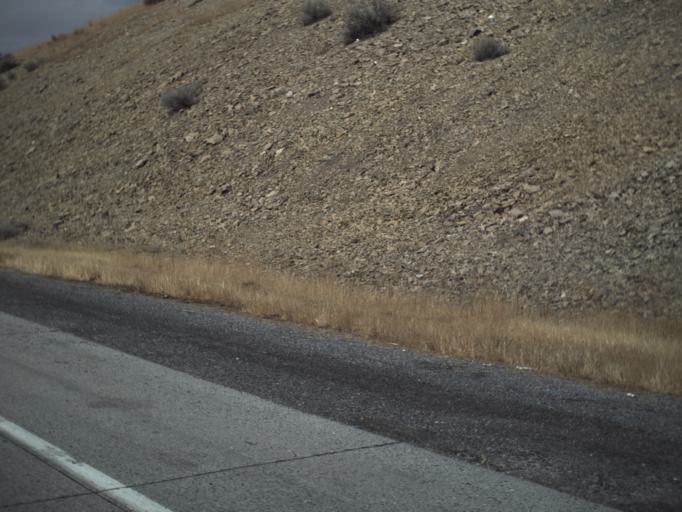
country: US
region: Utah
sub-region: Box Elder County
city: Garland
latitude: 41.8008
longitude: -112.3050
